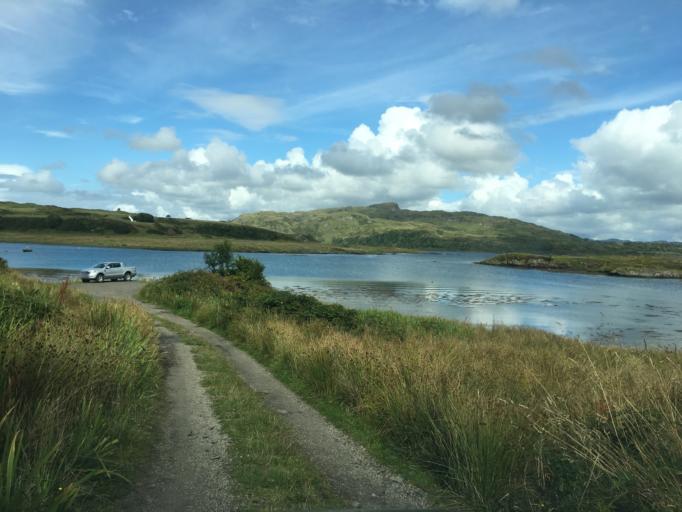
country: GB
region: Scotland
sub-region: Argyll and Bute
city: Oban
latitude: 56.2477
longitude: -5.6237
